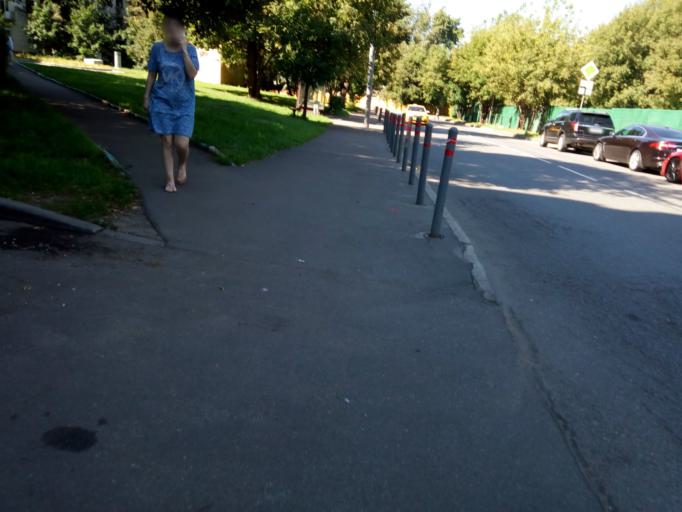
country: RU
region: Moscow
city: Sokol
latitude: 55.7744
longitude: 37.5293
